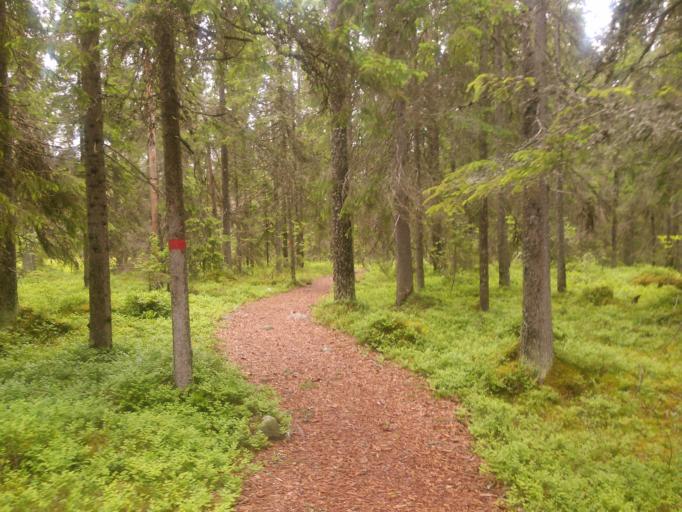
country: SE
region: Vaesterbotten
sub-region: Umea Kommun
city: Holmsund
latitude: 63.7818
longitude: 20.3475
